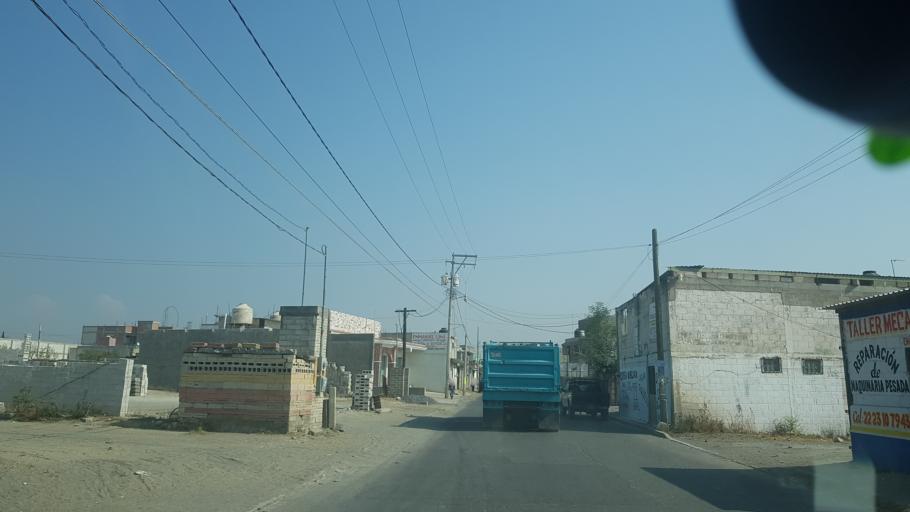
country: MX
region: Puebla
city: Nealtican
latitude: 19.0526
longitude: -98.4213
